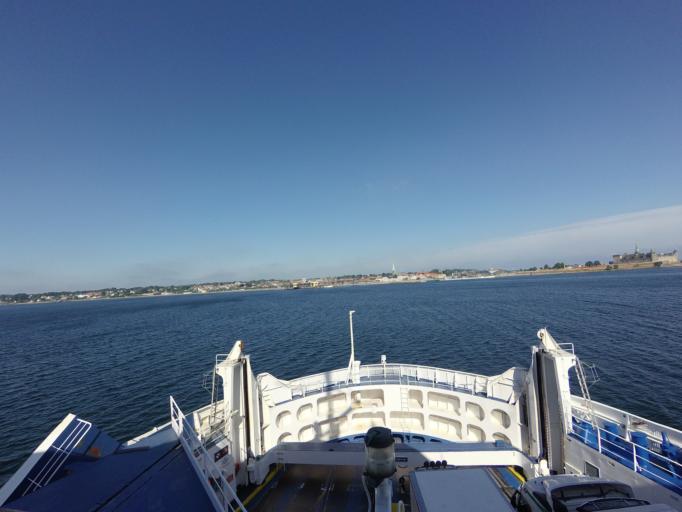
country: DK
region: Capital Region
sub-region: Helsingor Kommune
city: Helsingor
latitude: 56.0316
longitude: 12.6278
